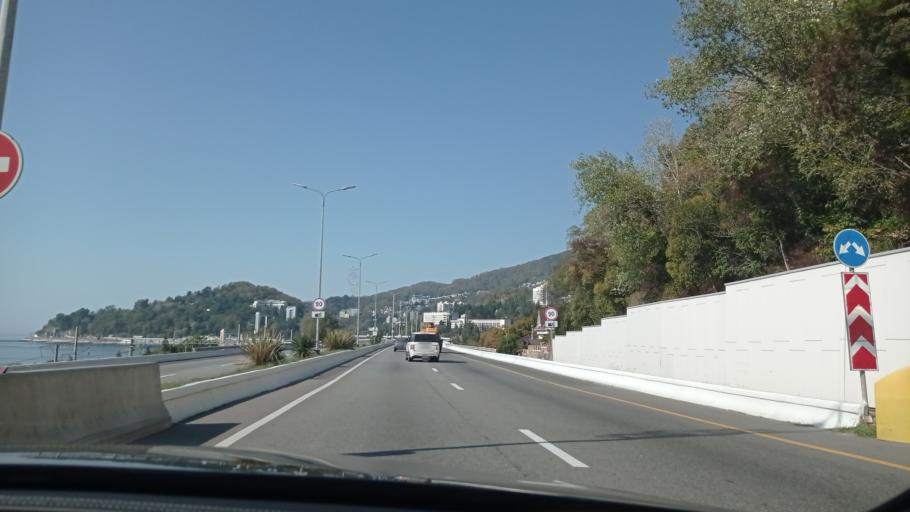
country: RU
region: Krasnodarskiy
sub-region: Sochi City
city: Khosta
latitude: 43.5057
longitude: 39.8711
